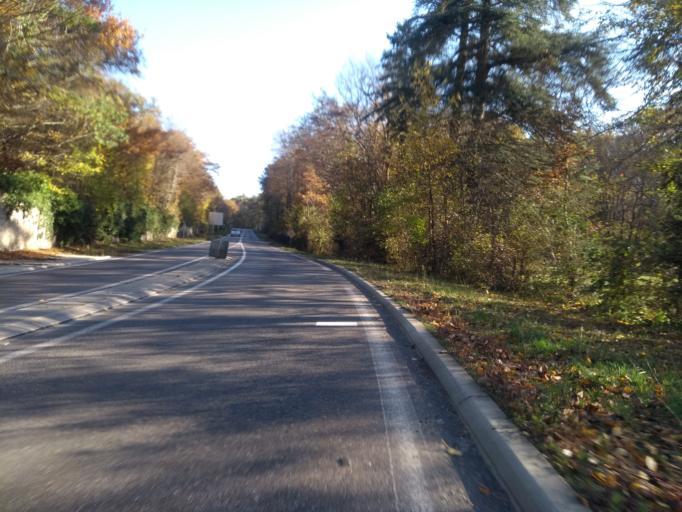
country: FR
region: Aquitaine
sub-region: Departement de la Gironde
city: Ayguemorte-les-Graves
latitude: 44.6938
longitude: -0.5088
